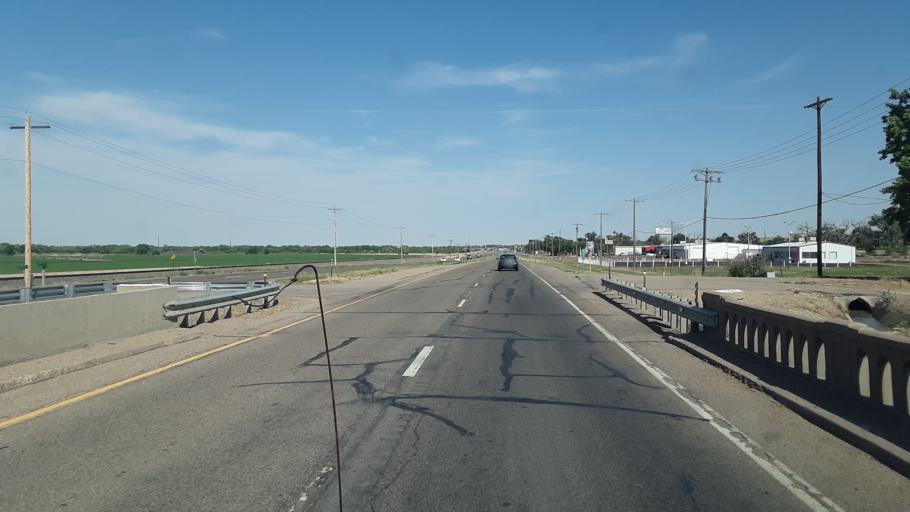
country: US
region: Colorado
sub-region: Otero County
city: La Junta
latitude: 37.9988
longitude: -103.5877
